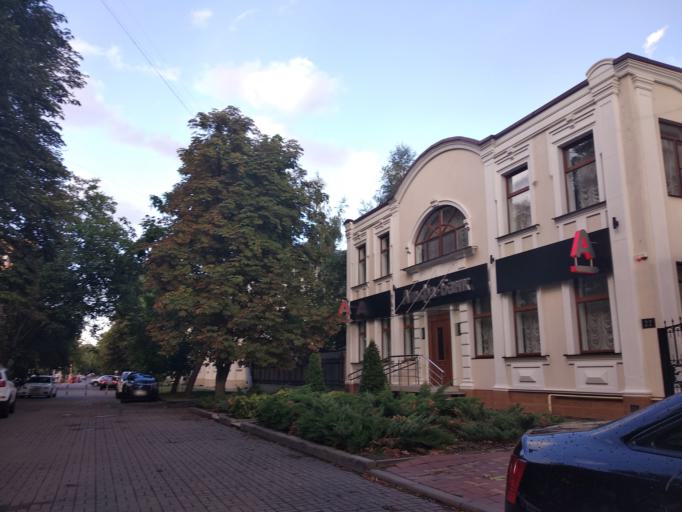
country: RU
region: Krasnodarskiy
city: Krasnodar
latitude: 45.0169
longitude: 38.9640
